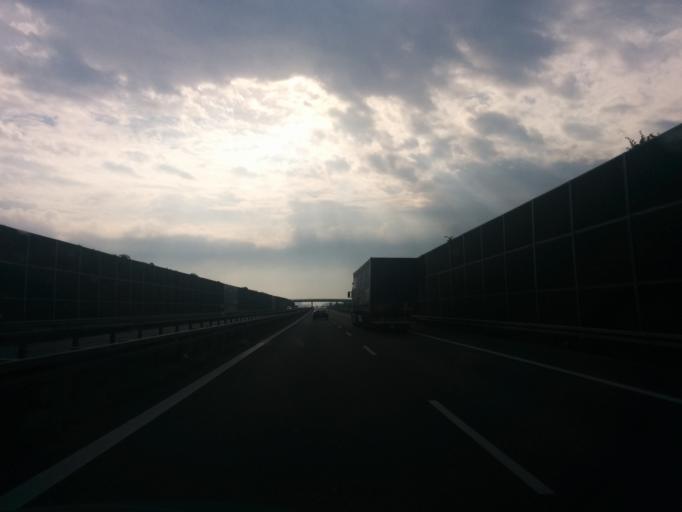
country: PL
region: Masovian Voivodeship
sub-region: Powiat radomski
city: Jedlinsk
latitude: 51.5471
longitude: 21.0505
